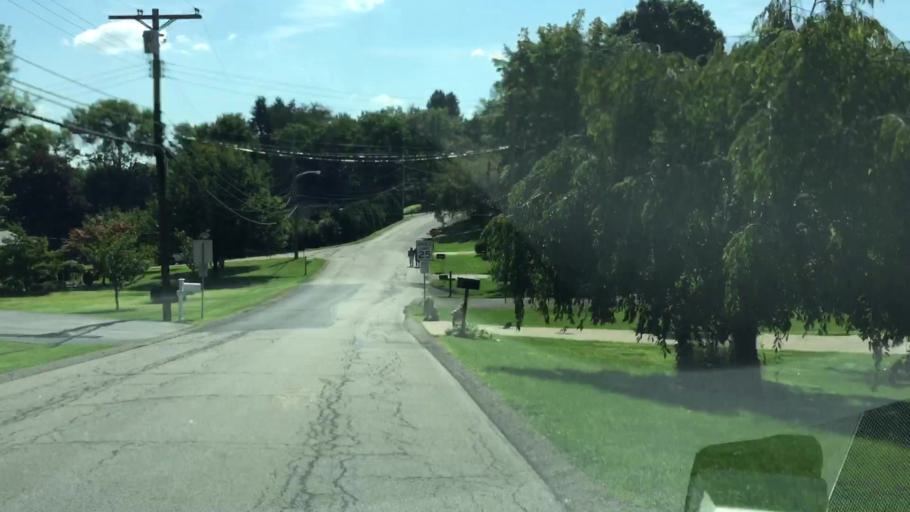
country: US
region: Pennsylvania
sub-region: Allegheny County
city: Carnot-Moon
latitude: 40.5059
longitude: -80.2163
